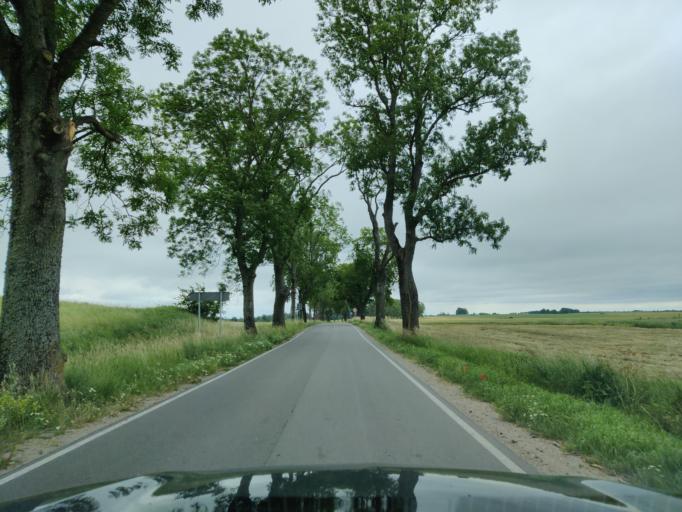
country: PL
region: Warmian-Masurian Voivodeship
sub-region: Powiat mragowski
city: Mikolajki
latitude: 53.8737
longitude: 21.5951
